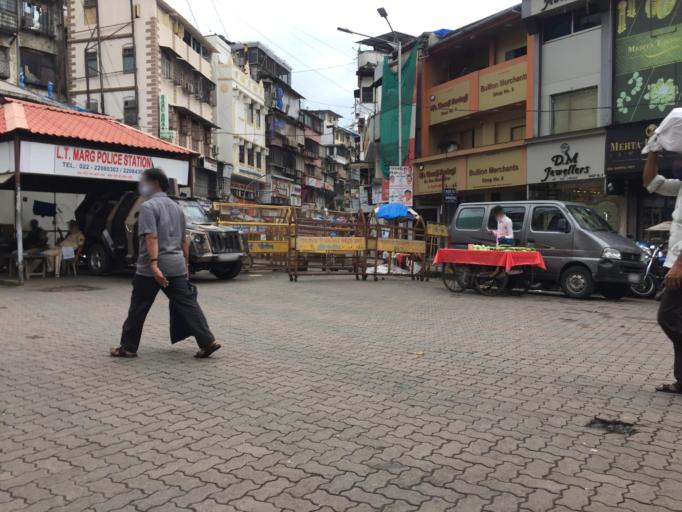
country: IN
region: Maharashtra
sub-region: Mumbai Suburban
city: Mumbai
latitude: 18.9525
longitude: 72.8314
